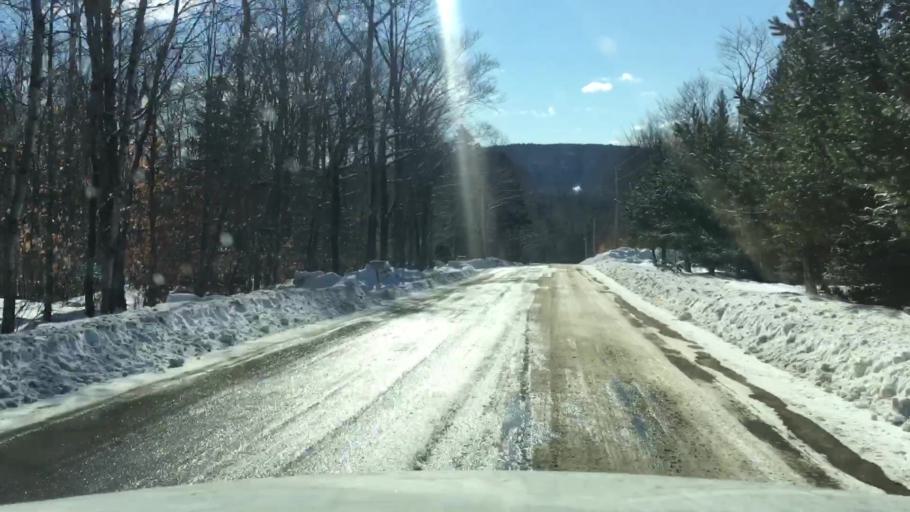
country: US
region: Maine
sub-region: Washington County
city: Calais
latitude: 45.0732
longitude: -67.5005
